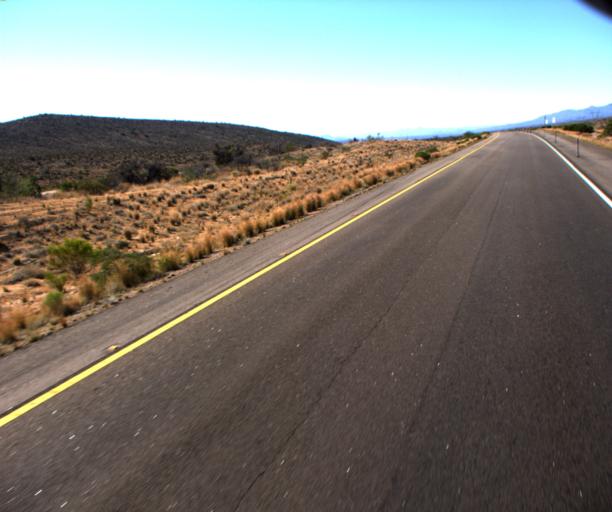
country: US
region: Arizona
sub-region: Mohave County
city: Kingman
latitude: 34.9550
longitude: -113.6694
